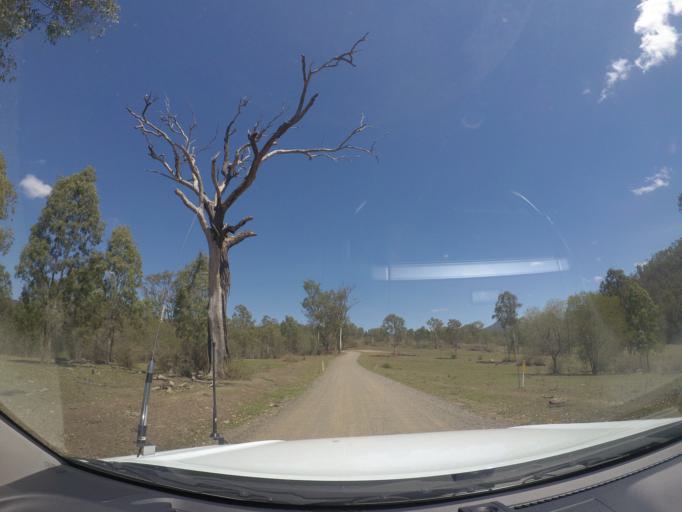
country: AU
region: Queensland
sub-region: Logan
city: Cedar Vale
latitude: -27.8597
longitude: 152.8579
